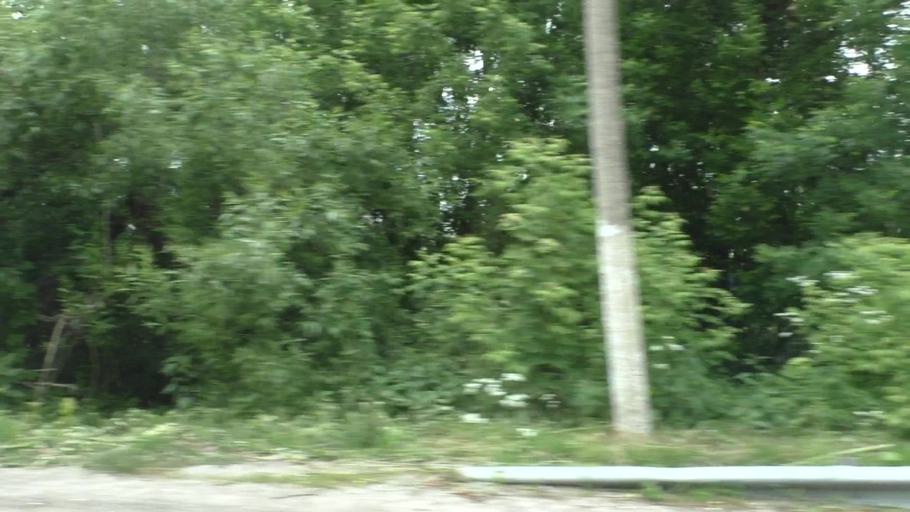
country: RU
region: Moskovskaya
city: Yegor'yevsk
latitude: 55.3959
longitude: 39.0159
